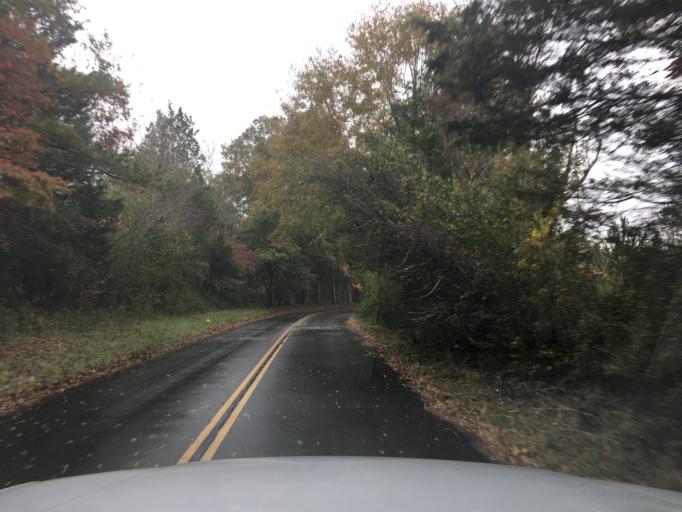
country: US
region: South Carolina
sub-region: Pickens County
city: Central
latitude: 34.7345
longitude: -82.7696
